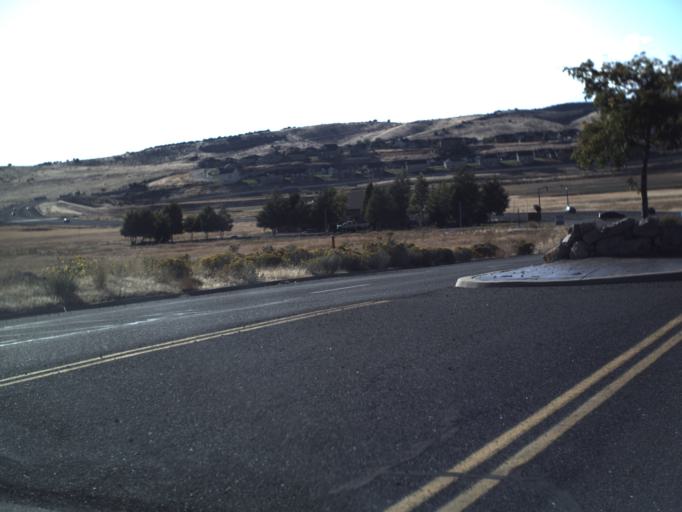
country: US
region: Utah
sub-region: Utah County
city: Santaquin
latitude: 39.9515
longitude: -111.8045
